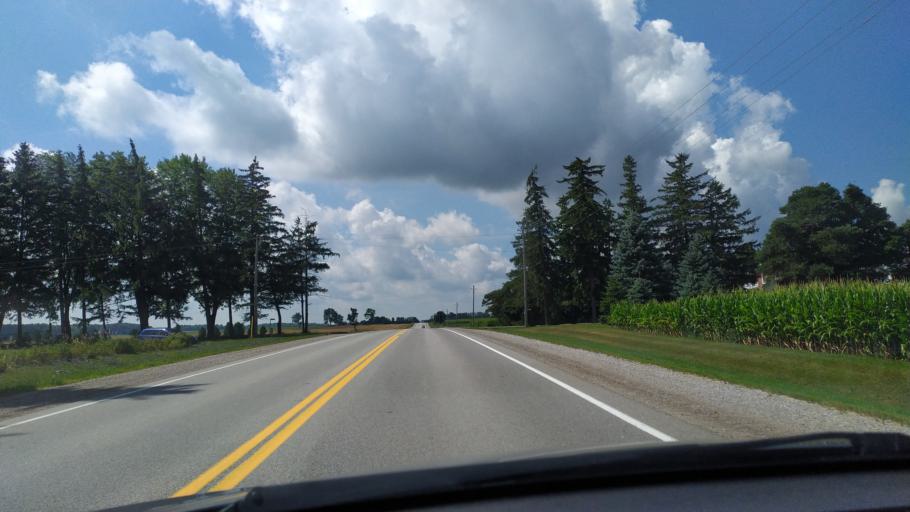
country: CA
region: Ontario
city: South Huron
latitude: 43.3624
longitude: -81.2815
